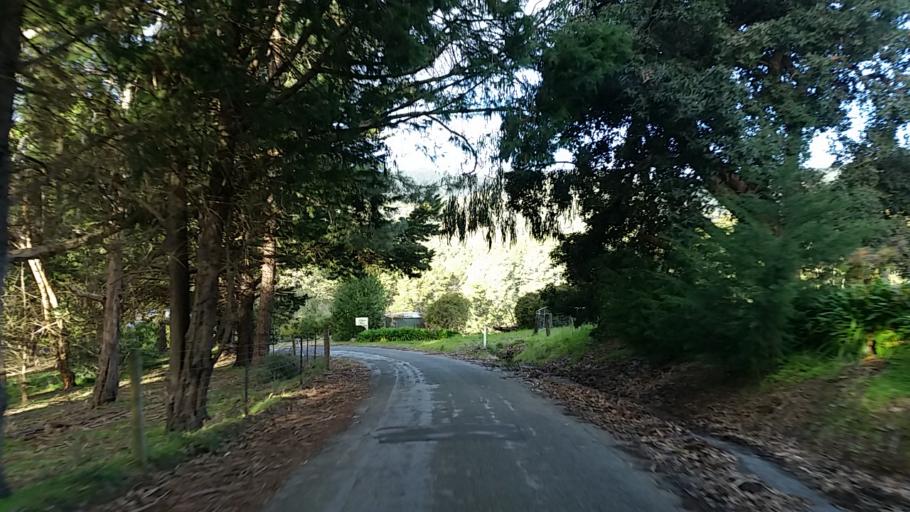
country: AU
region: South Australia
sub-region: Adelaide Hills
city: Adelaide Hills
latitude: -34.9355
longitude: 138.7670
